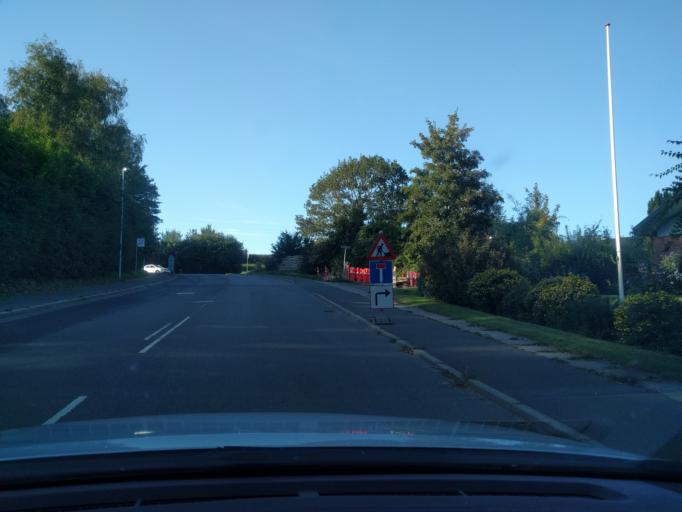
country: DK
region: Central Jutland
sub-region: Horsens Kommune
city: Horsens
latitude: 55.8694
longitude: 9.8987
